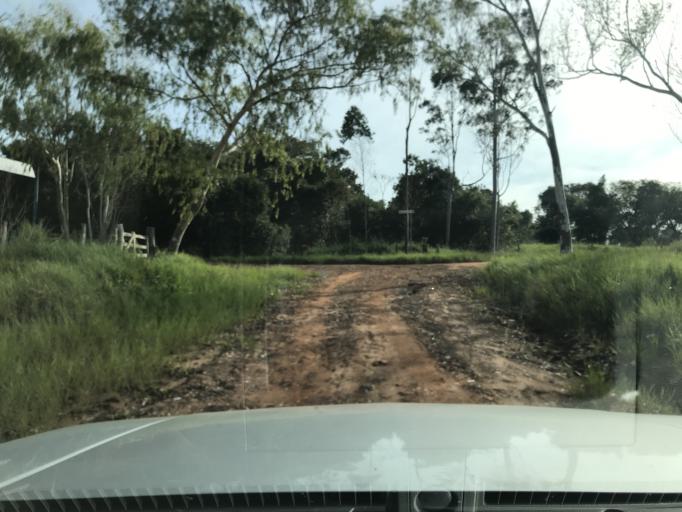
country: BR
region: Mato Grosso do Sul
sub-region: Iguatemi
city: Iguatemi
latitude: -23.6453
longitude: -54.5766
